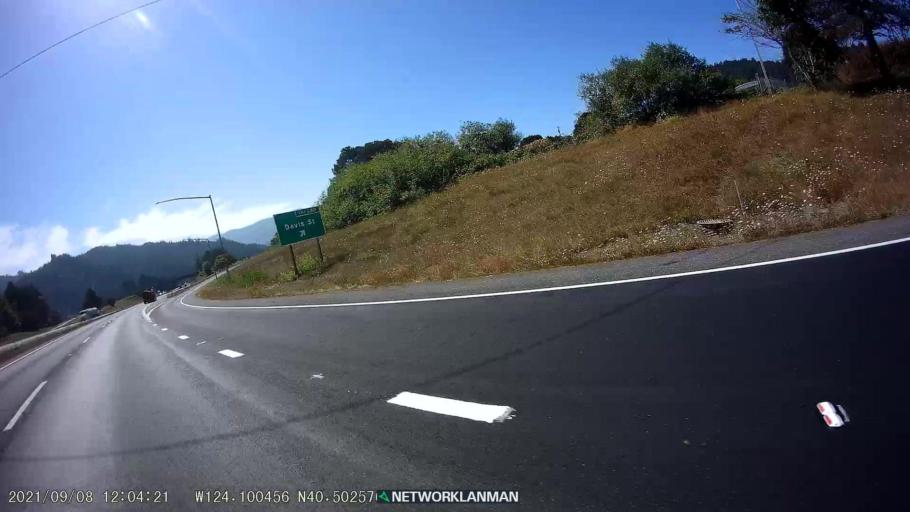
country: US
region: California
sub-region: Humboldt County
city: Rio Dell
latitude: 40.5031
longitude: -124.1000
